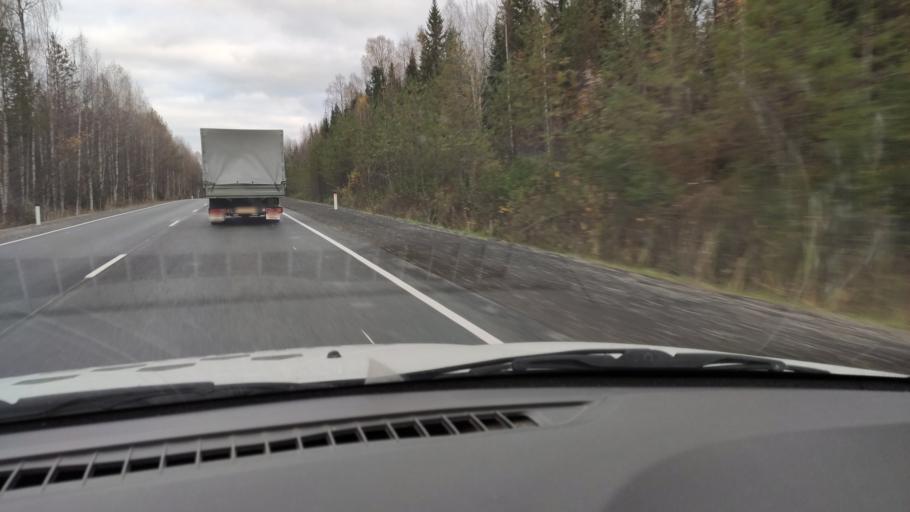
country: RU
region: Kirov
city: Chernaya Kholunitsa
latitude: 58.8719
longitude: 51.5262
